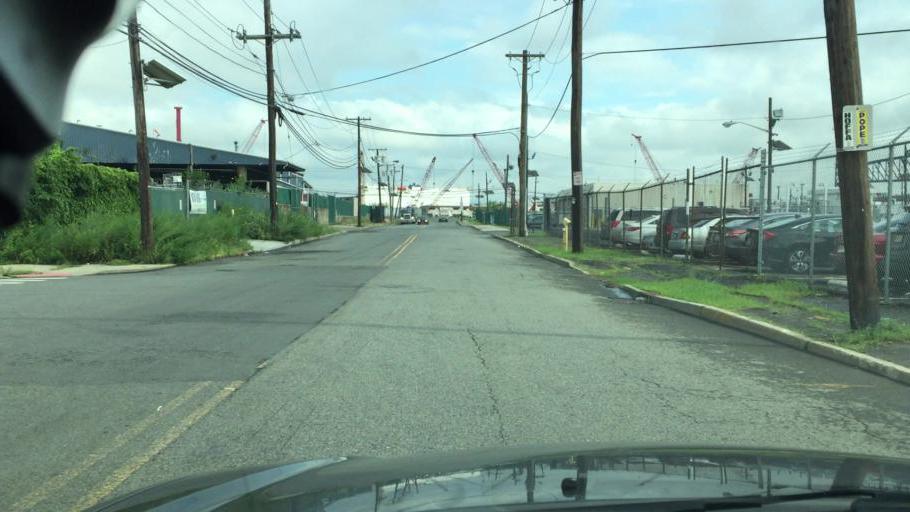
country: US
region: New Jersey
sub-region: Union County
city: Elizabeth
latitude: 40.6452
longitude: -74.1969
